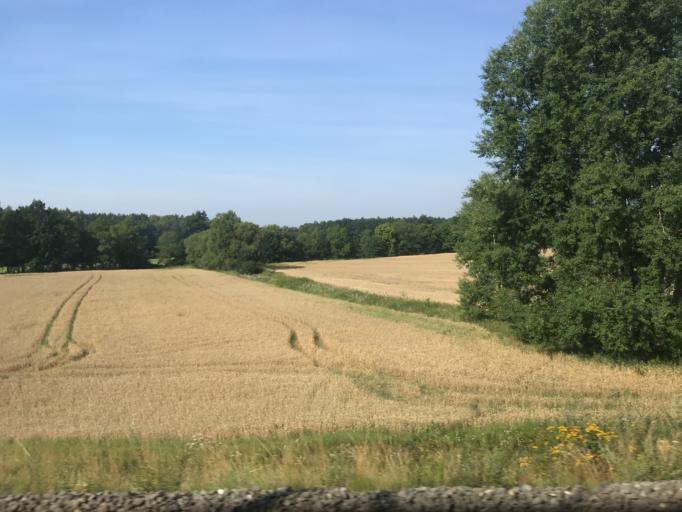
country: CZ
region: Jihocesky
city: Chotoviny
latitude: 49.4597
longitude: 14.6807
